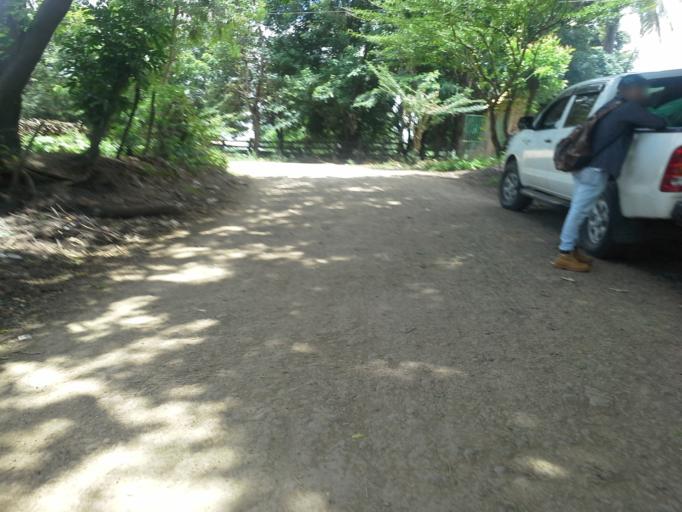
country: NI
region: Matagalpa
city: Ciudad Dario
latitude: 12.6995
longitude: -86.0510
